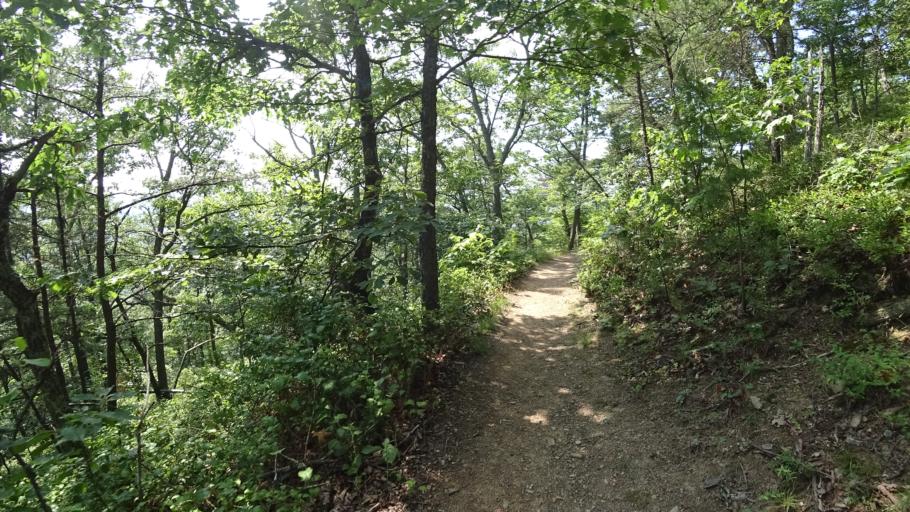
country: US
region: Virginia
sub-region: Smyth County
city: Marion
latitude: 36.8827
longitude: -81.5119
